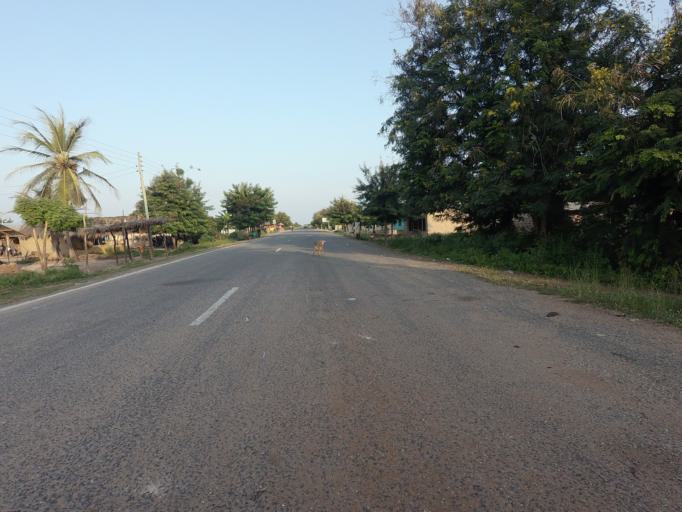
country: GH
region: Volta
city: Anloga
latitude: 5.8929
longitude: 0.7172
